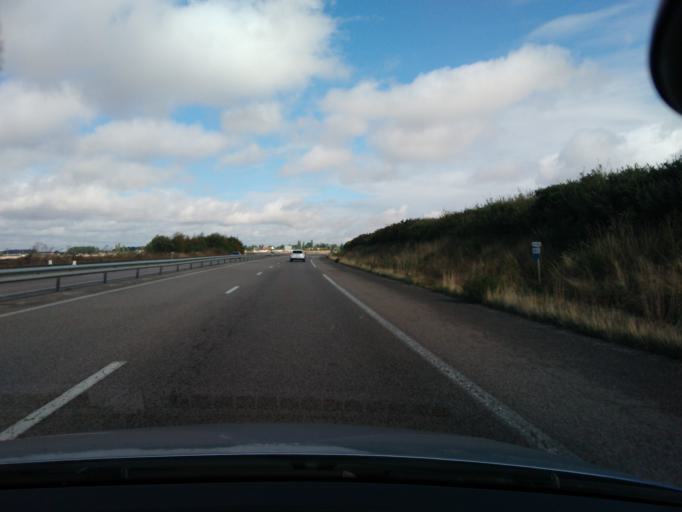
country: FR
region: Haute-Normandie
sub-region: Departement de l'Eure
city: Damville
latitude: 48.8974
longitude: 1.1713
